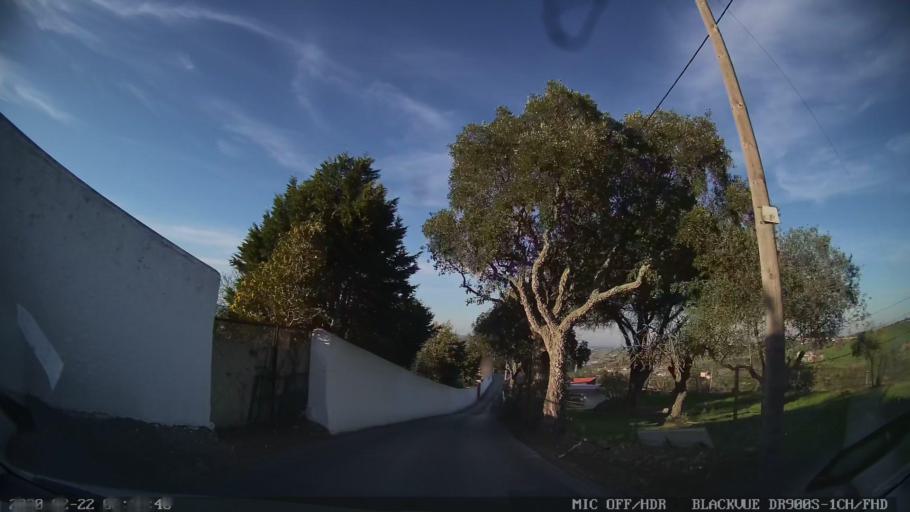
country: PT
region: Lisbon
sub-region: Vila Franca de Xira
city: Vila Franca de Xira
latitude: 38.9807
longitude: -9.0148
